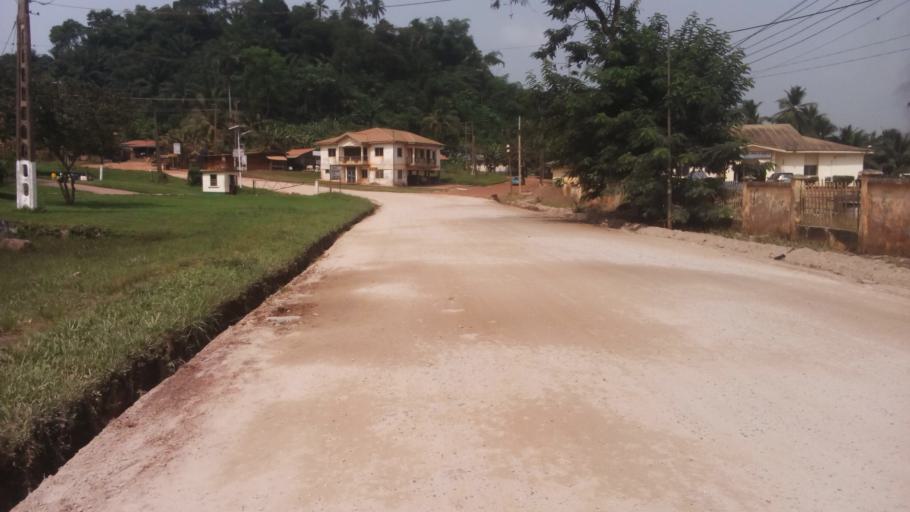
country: GH
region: Western
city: Tarkwa
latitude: 5.2994
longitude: -1.9994
